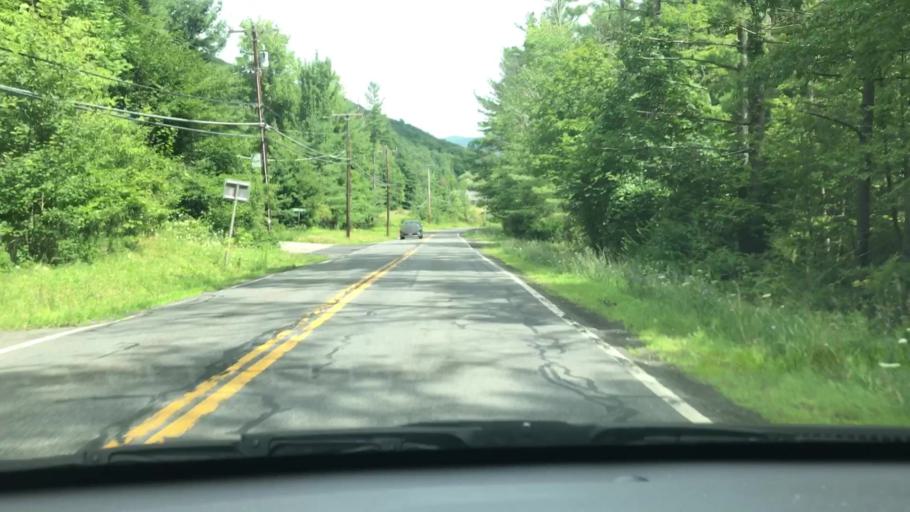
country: US
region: New York
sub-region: Ulster County
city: Shokan
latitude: 41.9963
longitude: -74.2772
